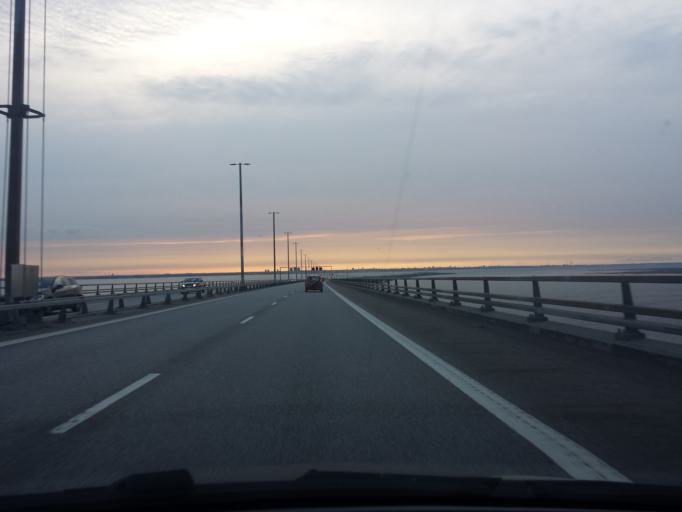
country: DK
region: Capital Region
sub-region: Dragor Kommune
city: Dragor
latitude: 55.5802
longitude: 12.8057
